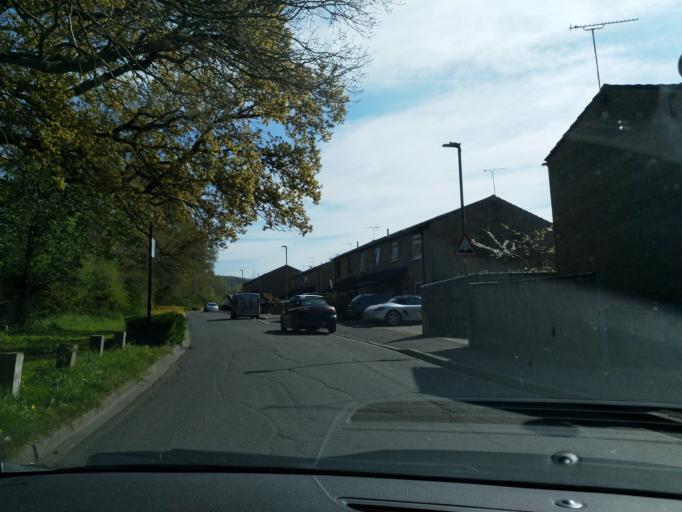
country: GB
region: England
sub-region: Oxfordshire
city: Cowley
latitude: 51.7461
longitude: -1.2000
